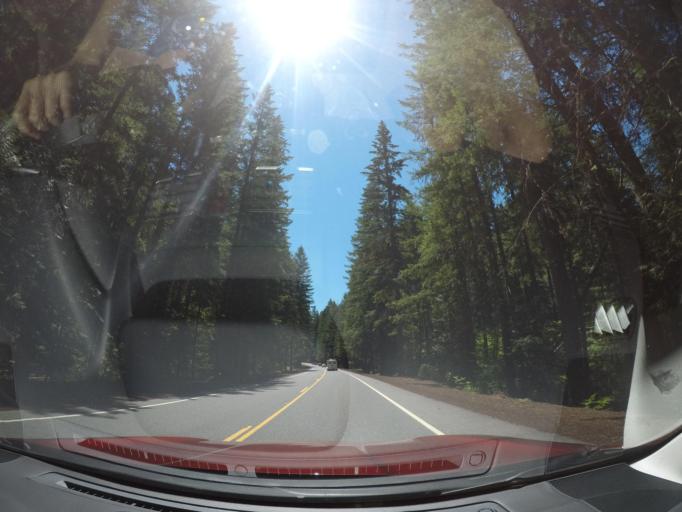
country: US
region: Oregon
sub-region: Deschutes County
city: Sisters
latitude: 44.6439
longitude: -121.9447
